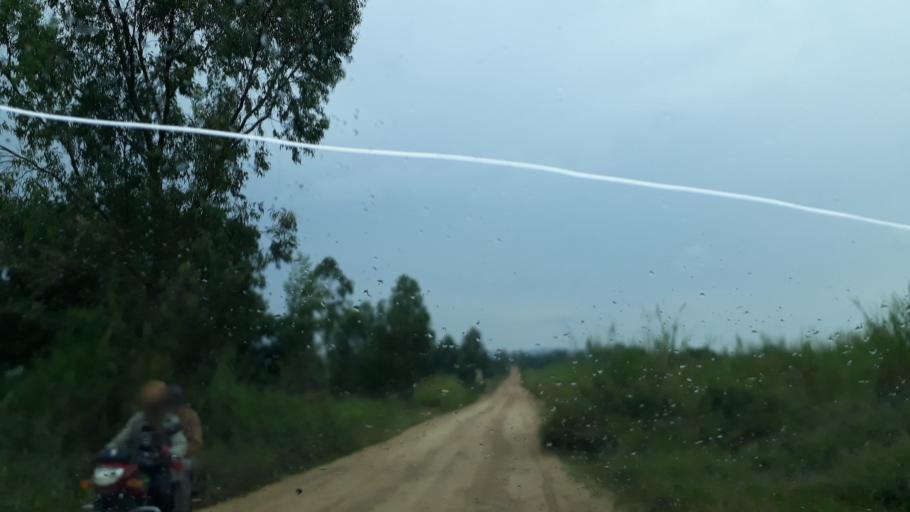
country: CD
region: Eastern Province
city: Bunia
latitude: 1.5092
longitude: 30.2381
